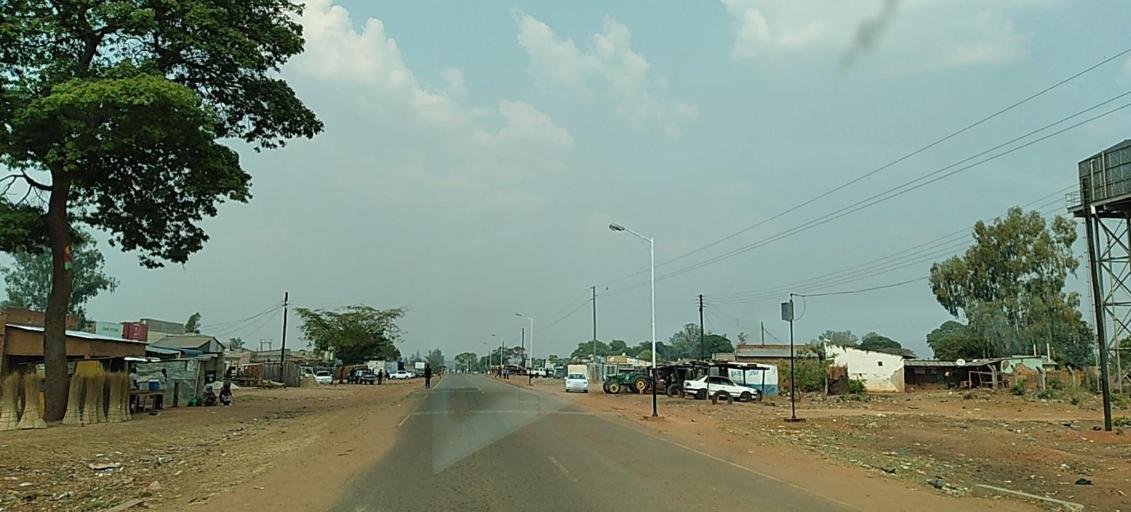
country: ZM
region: North-Western
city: Kabompo
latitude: -13.5943
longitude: 24.1978
